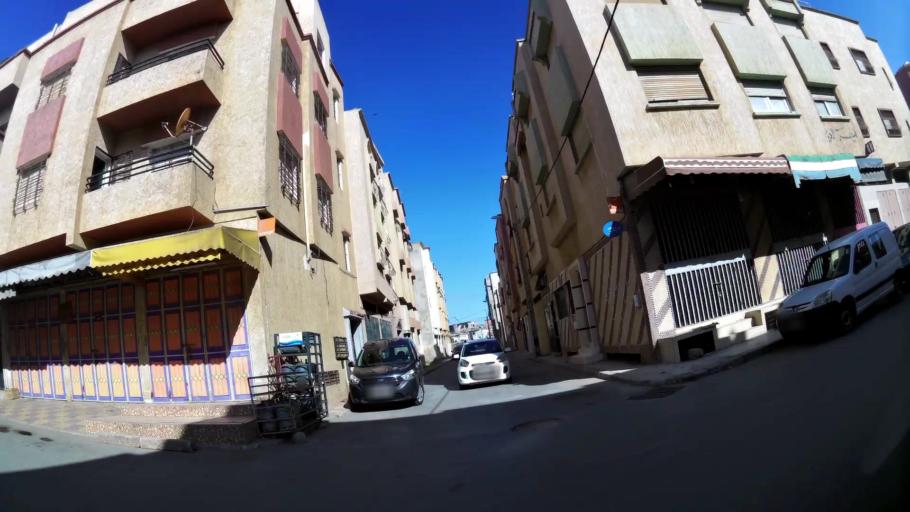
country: MA
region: Rabat-Sale-Zemmour-Zaer
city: Sale
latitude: 34.0565
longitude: -6.8111
